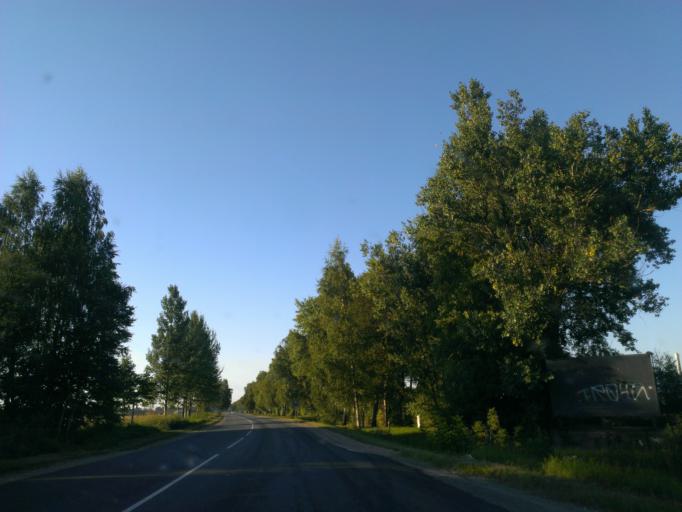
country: LV
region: Adazi
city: Adazi
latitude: 57.0639
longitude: 24.3235
